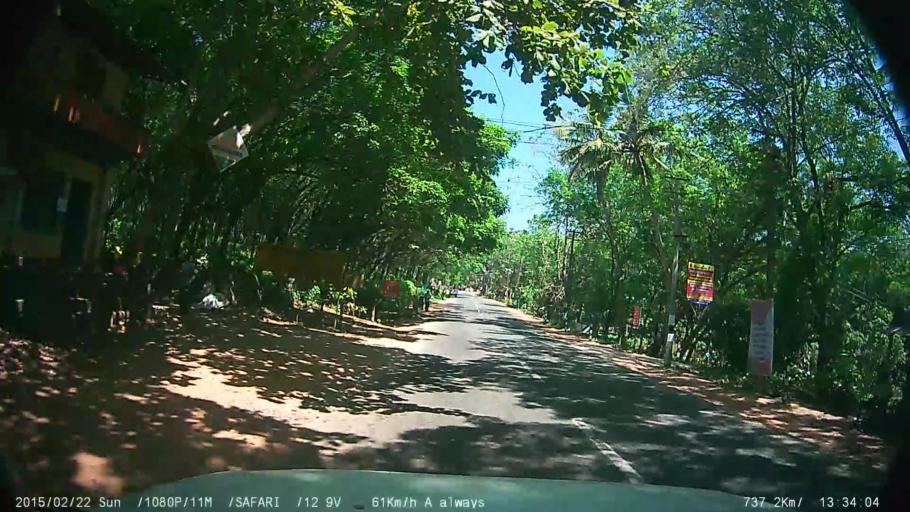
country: IN
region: Kerala
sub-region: Kottayam
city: Changanacheri
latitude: 9.4808
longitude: 76.5967
